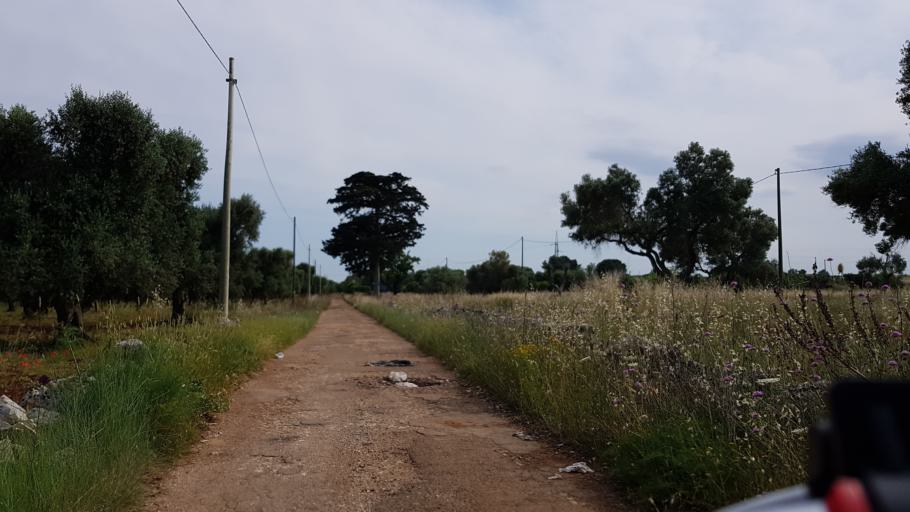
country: IT
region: Apulia
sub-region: Provincia di Brindisi
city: San Vito dei Normanni
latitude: 40.6482
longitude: 17.7708
